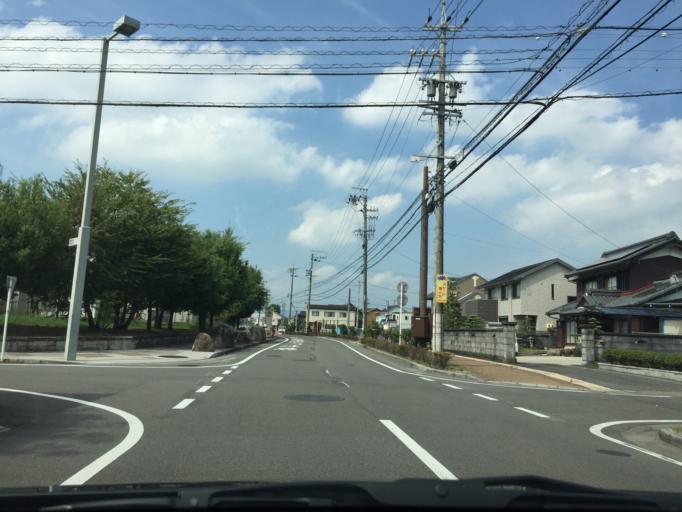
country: JP
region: Gifu
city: Ogaki
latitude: 35.3700
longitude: 136.6395
